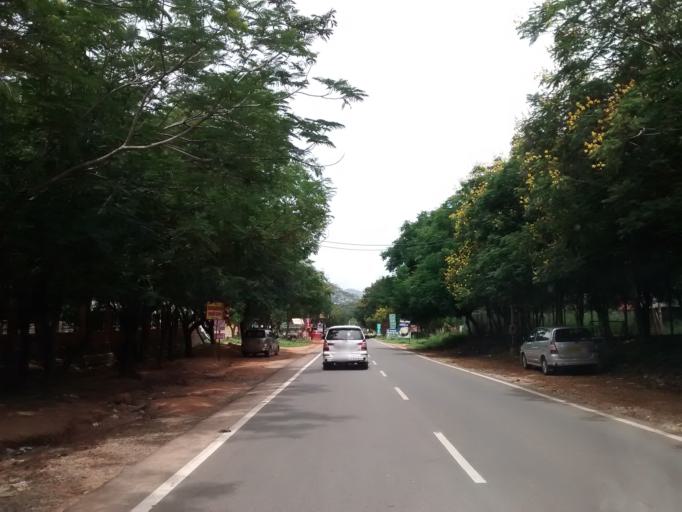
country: IN
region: Andhra Pradesh
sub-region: Chittoor
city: Narasingapuram
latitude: 13.6242
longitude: 79.3653
